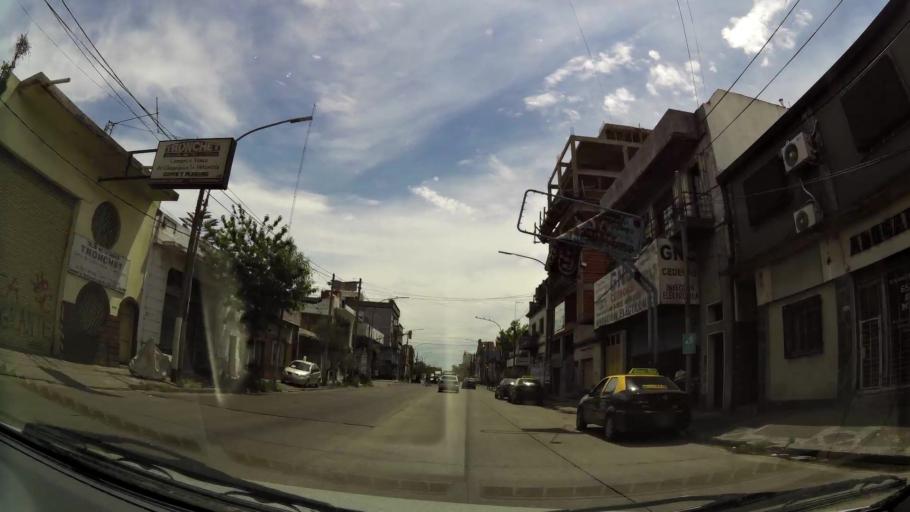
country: AR
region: Buenos Aires
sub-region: Partido de Lanus
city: Lanus
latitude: -34.6723
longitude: -58.4122
